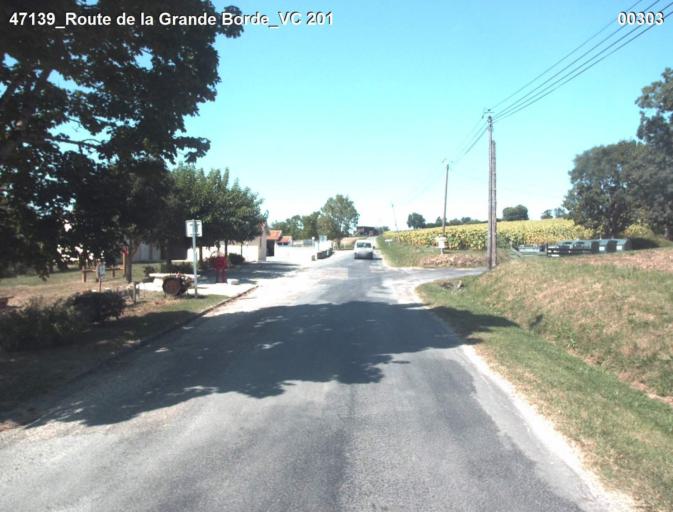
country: FR
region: Aquitaine
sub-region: Departement du Lot-et-Garonne
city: Nerac
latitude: 44.0650
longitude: 0.3931
